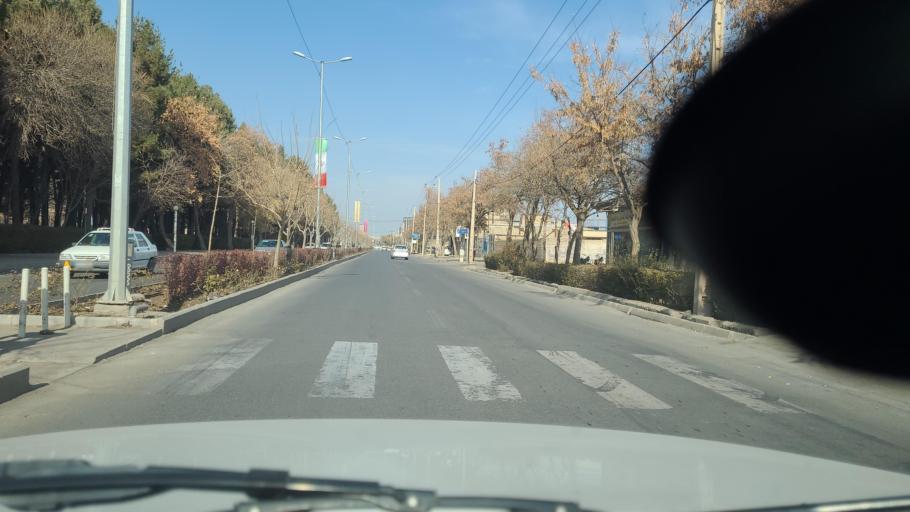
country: IR
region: Razavi Khorasan
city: Fariman
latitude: 35.6917
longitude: 59.8441
